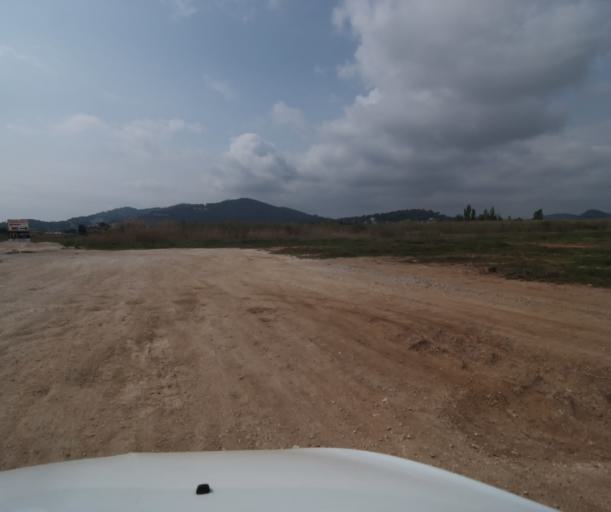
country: FR
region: Provence-Alpes-Cote d'Azur
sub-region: Departement du Var
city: Hyeres
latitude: 43.0861
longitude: 6.1407
